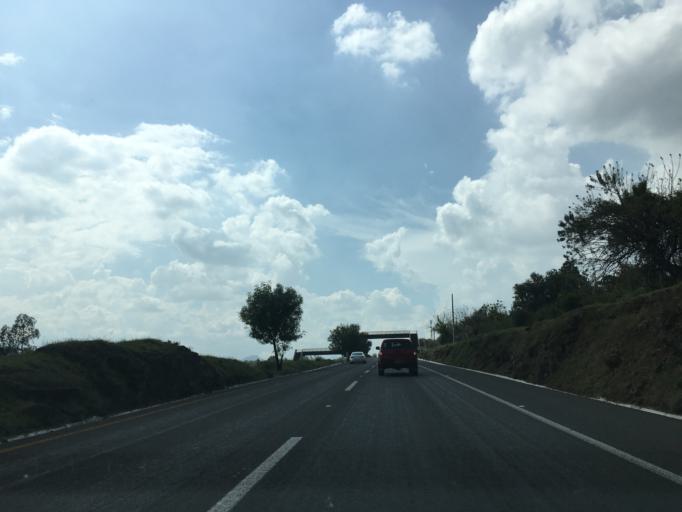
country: MX
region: Michoacan
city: Acuitzio del Canje
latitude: 19.5554
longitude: -101.3423
